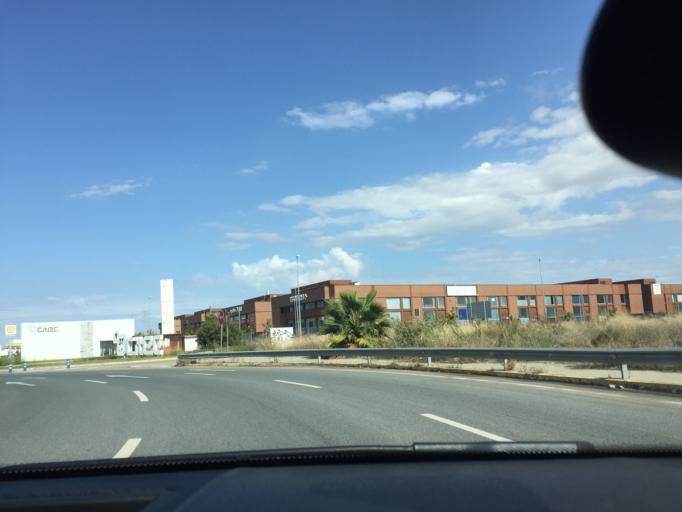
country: ES
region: Andalusia
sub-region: Provincia de Sevilla
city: Gelves
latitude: 37.3222
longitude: -6.0311
